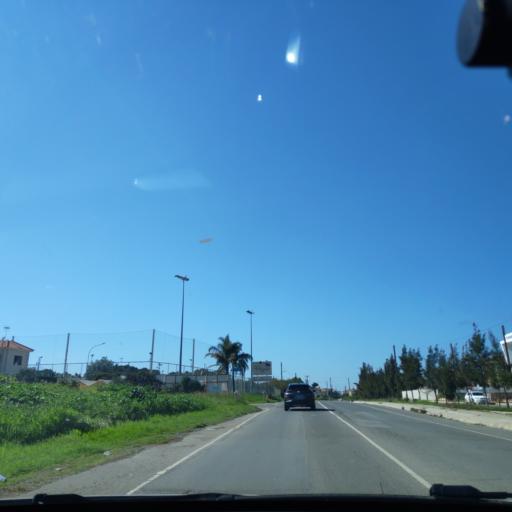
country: CY
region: Lefkosia
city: Tseri
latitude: 35.1125
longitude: 33.3295
